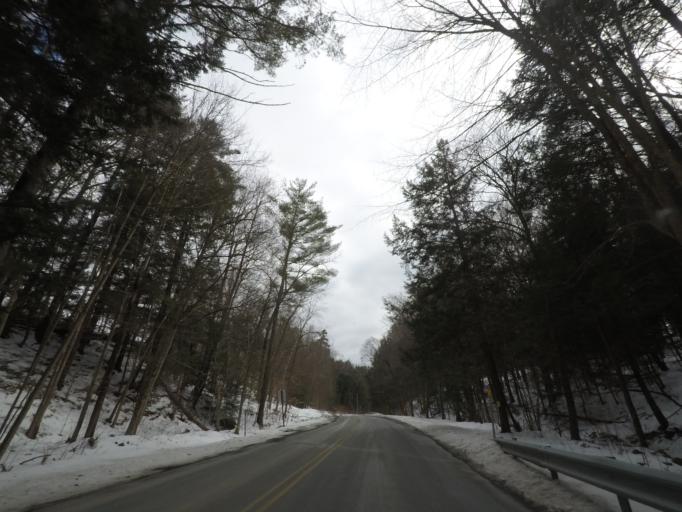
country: US
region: New York
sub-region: Rensselaer County
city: Hoosick Falls
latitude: 42.8811
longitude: -73.4151
